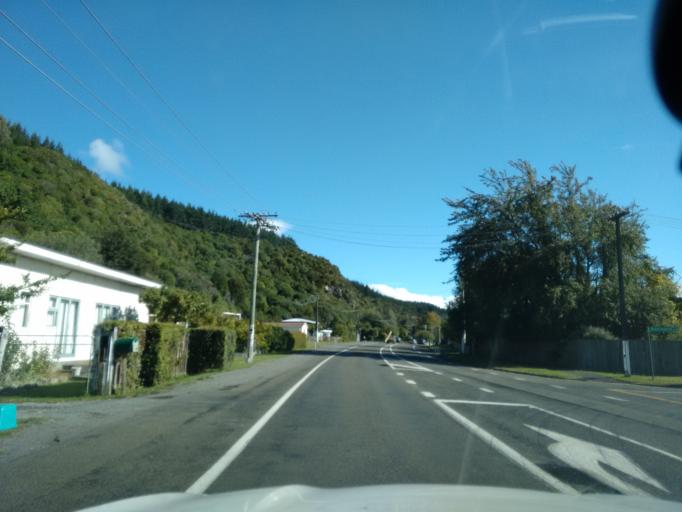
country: NZ
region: Waikato
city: Turangi
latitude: -38.9321
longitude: 175.8759
